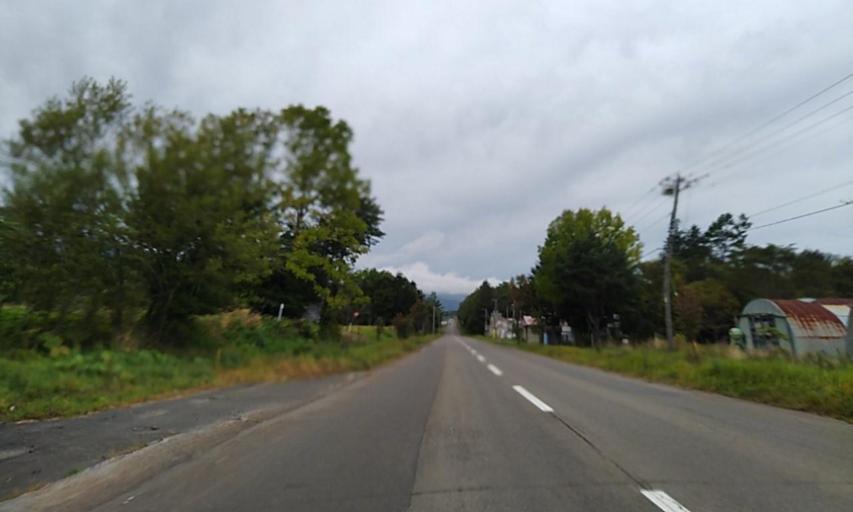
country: JP
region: Hokkaido
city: Bihoro
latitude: 43.5559
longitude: 144.3278
